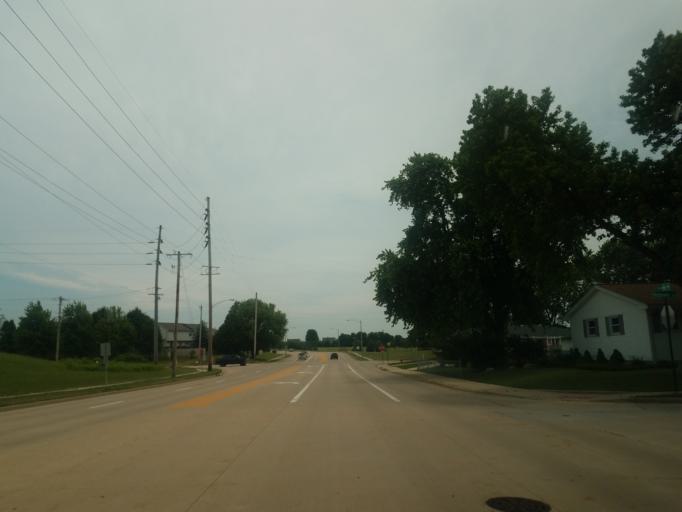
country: US
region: Illinois
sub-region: McLean County
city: Normal
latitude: 40.5186
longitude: -88.9437
